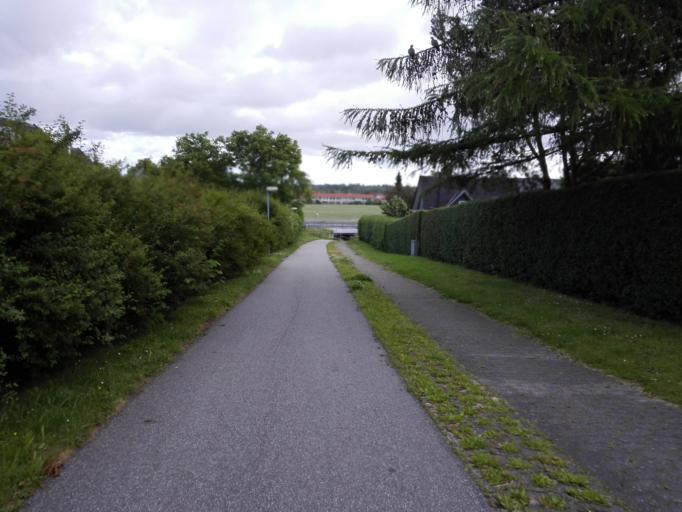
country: DK
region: Capital Region
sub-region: Frederikssund Kommune
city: Slangerup
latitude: 55.8387
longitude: 12.1763
